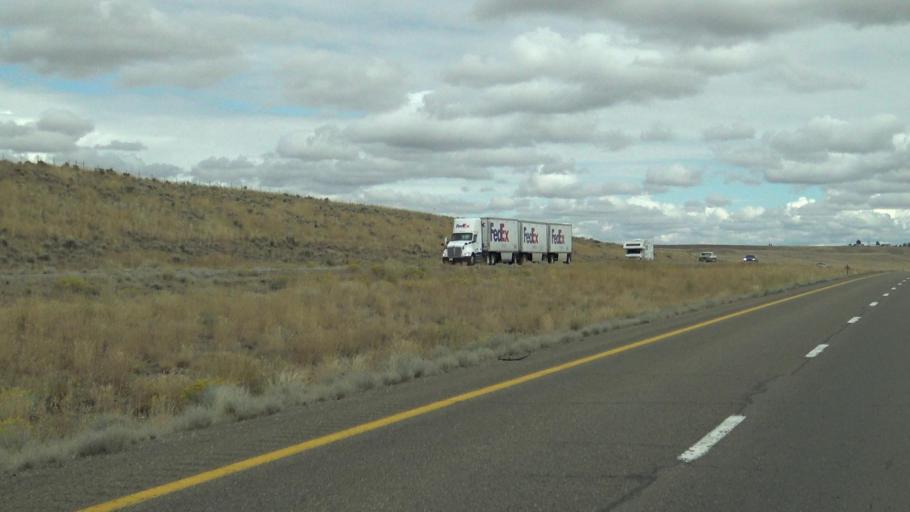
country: US
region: Nevada
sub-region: Elko County
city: Elko
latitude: 40.9086
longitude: -115.6970
